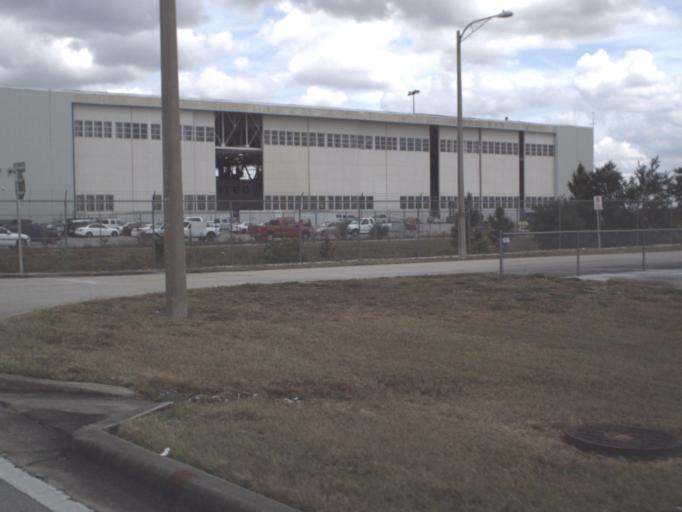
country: US
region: Florida
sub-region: Orange County
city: Taft
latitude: 28.4228
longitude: -81.3339
